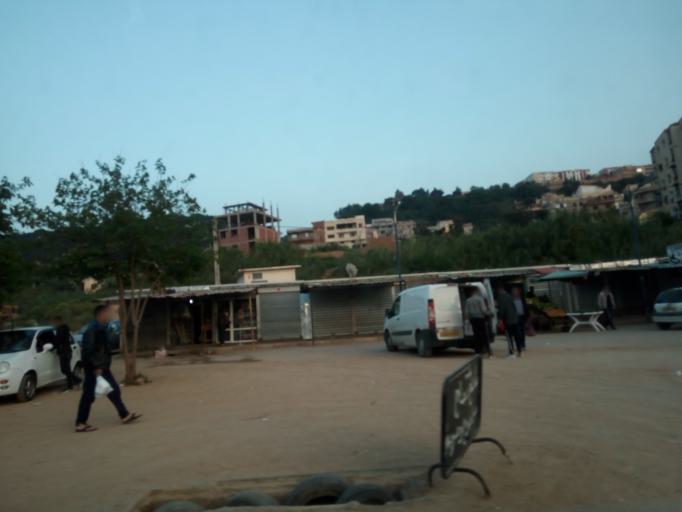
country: DZ
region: Tipaza
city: Bou Ismail
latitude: 36.6264
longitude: 2.6614
